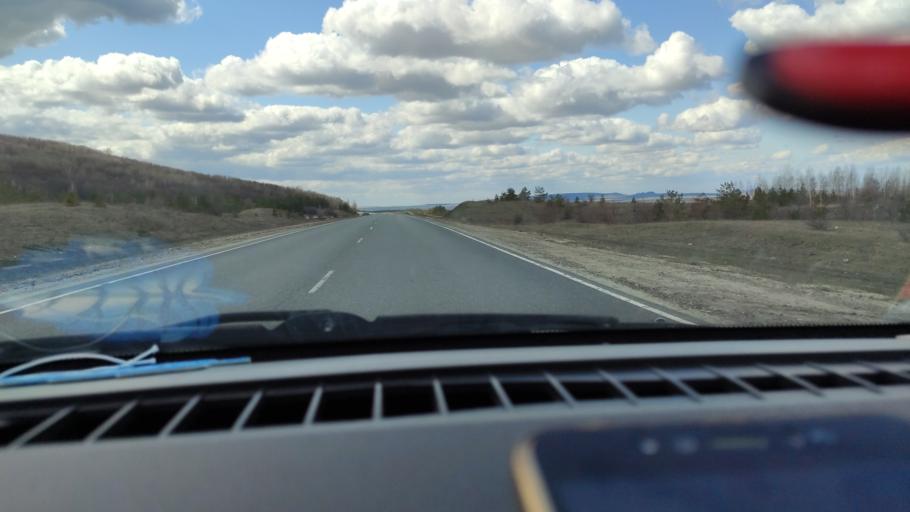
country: RU
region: Saratov
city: Alekseyevka
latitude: 52.3937
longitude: 47.9798
